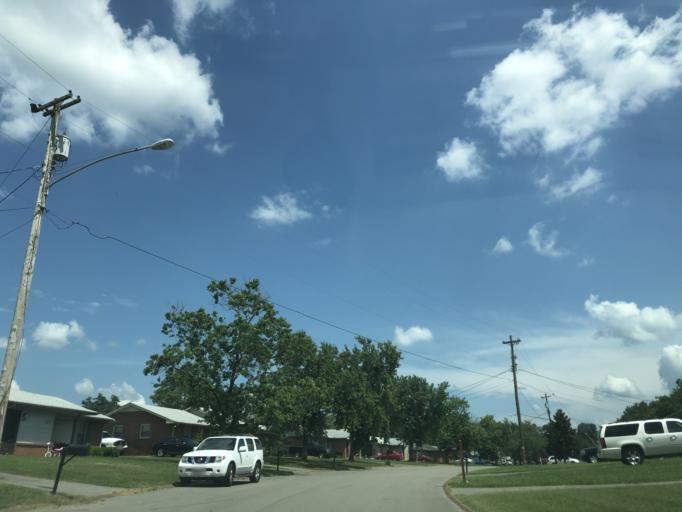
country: US
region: Tennessee
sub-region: Davidson County
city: Lakewood
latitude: 36.1982
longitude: -86.6141
